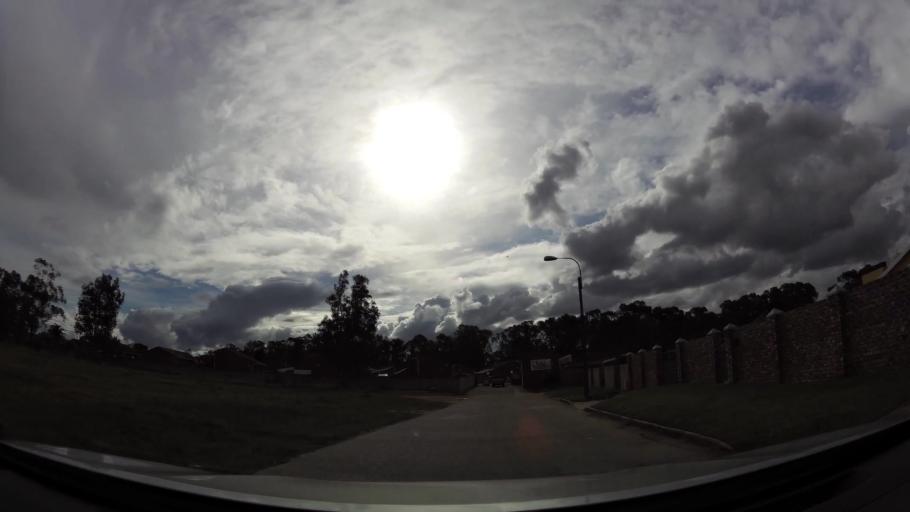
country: ZA
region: Eastern Cape
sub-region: Nelson Mandela Bay Metropolitan Municipality
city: Port Elizabeth
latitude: -33.9353
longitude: 25.4945
